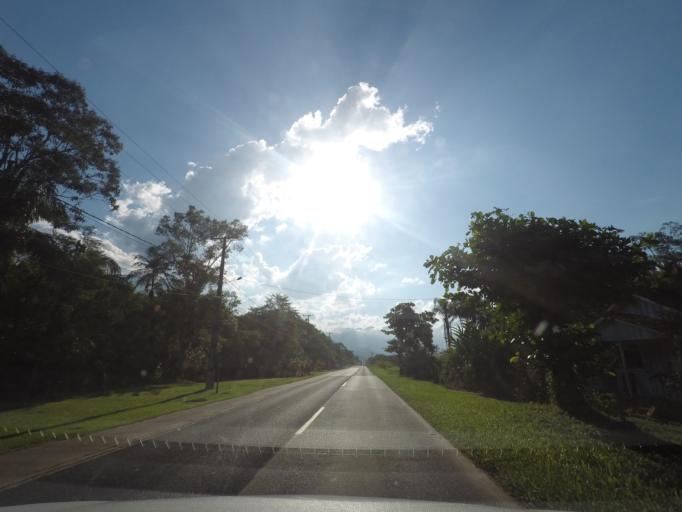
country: BR
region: Parana
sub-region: Antonina
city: Antonina
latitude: -25.4627
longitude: -48.8518
